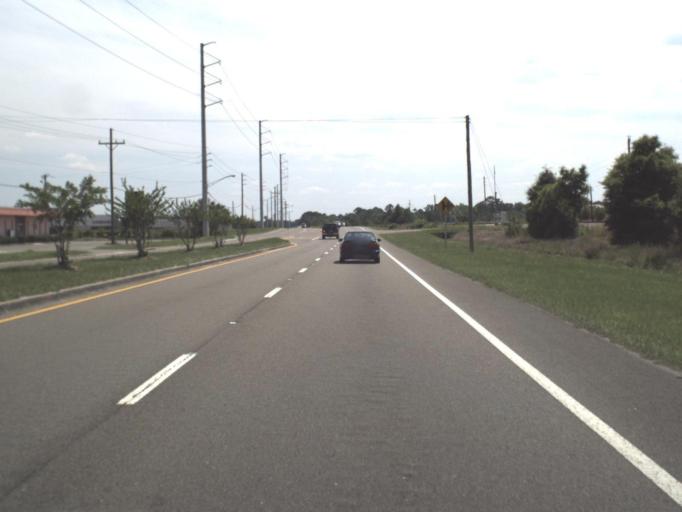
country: US
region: Florida
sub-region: Duval County
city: Jacksonville
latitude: 30.4260
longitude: -81.6464
